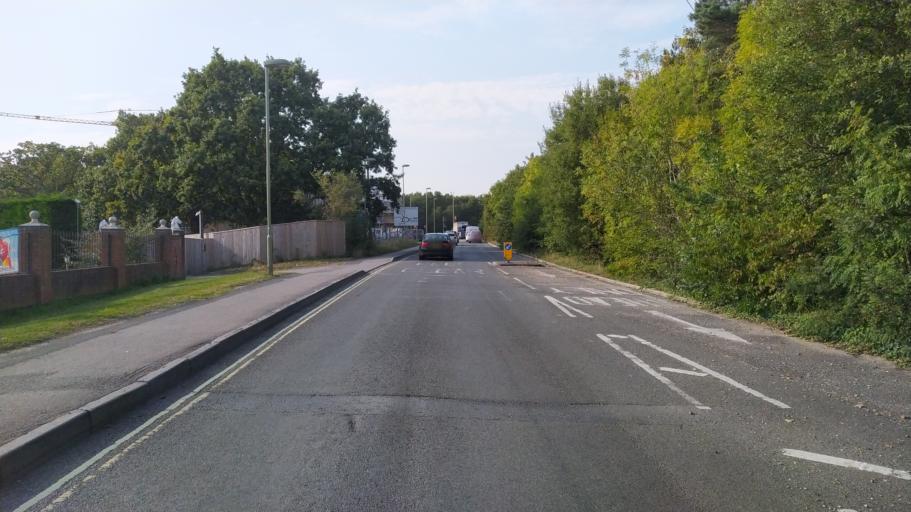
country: GB
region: England
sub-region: Hampshire
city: Botley
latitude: 50.8672
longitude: -1.2527
